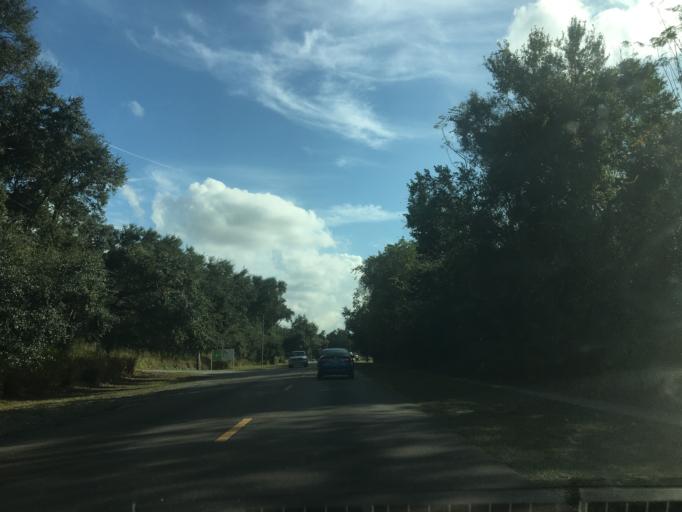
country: US
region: Florida
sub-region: Hillsborough County
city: Temple Terrace
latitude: 28.0133
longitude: -82.4309
